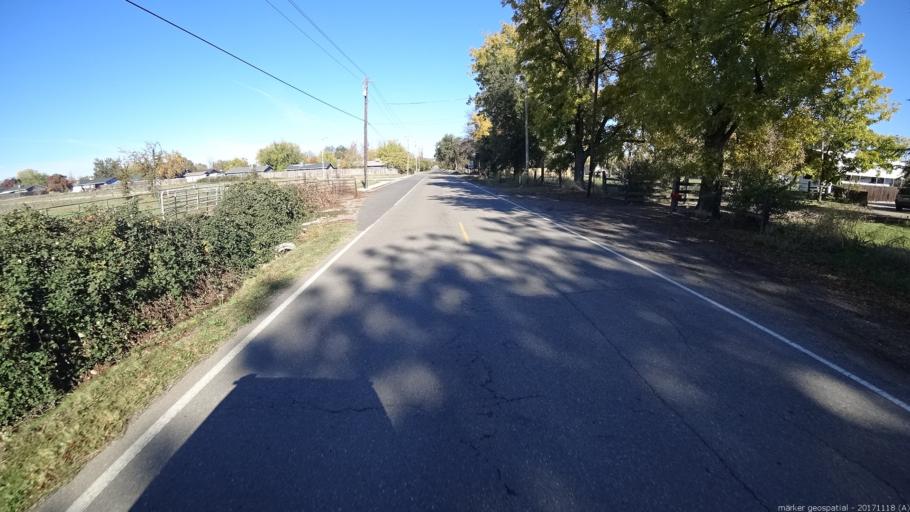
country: US
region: California
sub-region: Shasta County
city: Cottonwood
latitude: 40.3924
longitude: -122.2741
